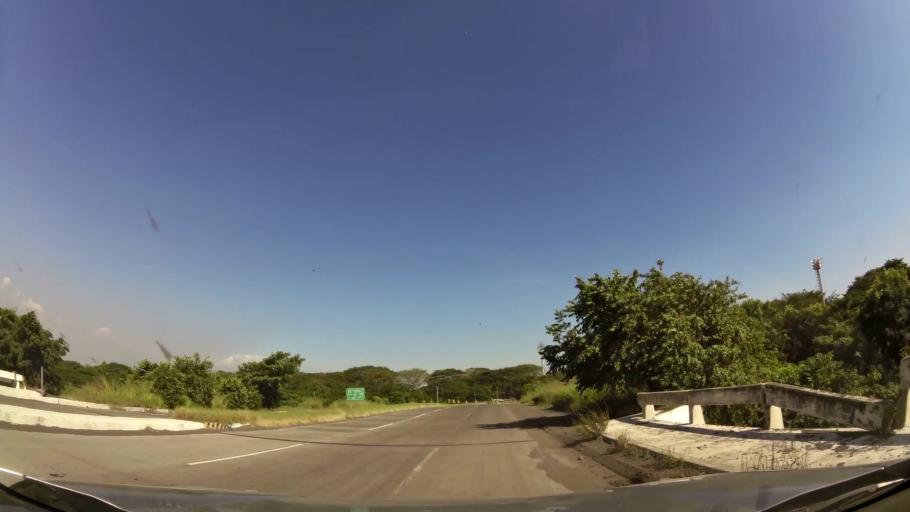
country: GT
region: Escuintla
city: Puerto San Jose
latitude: 13.9396
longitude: -90.7882
